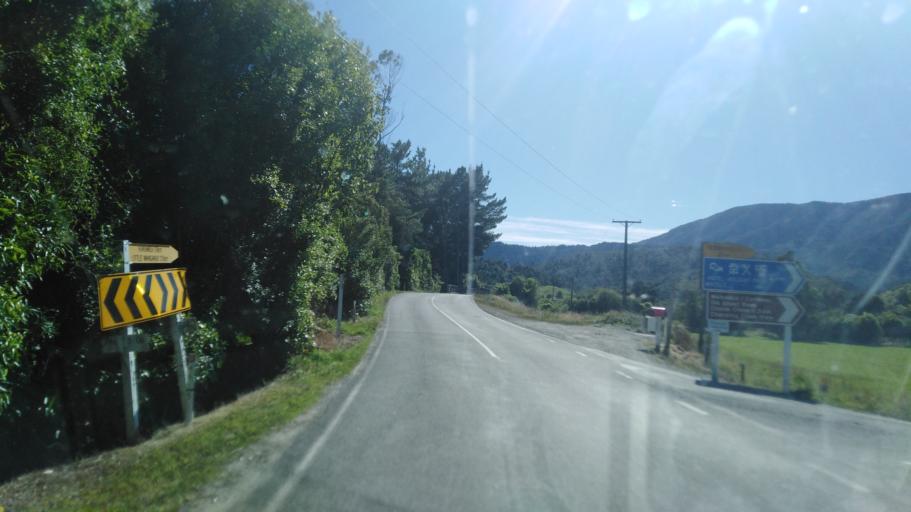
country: NZ
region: West Coast
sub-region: Buller District
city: Westport
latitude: -41.5301
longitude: 171.9657
